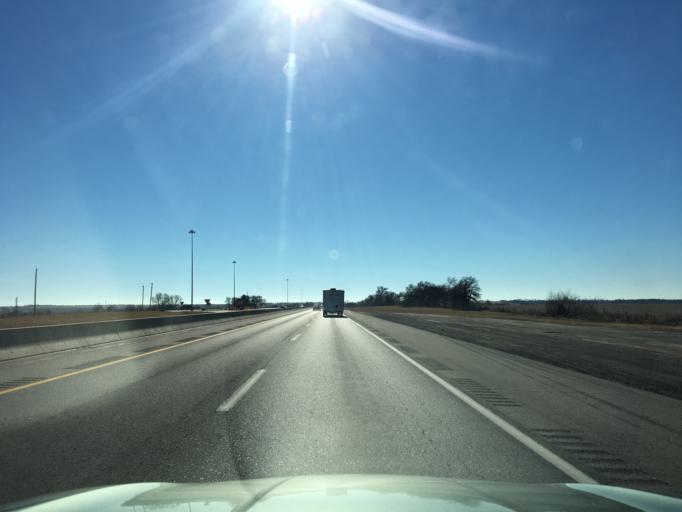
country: US
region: Oklahoma
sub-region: Kay County
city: Blackwell
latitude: 37.0269
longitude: -97.3383
